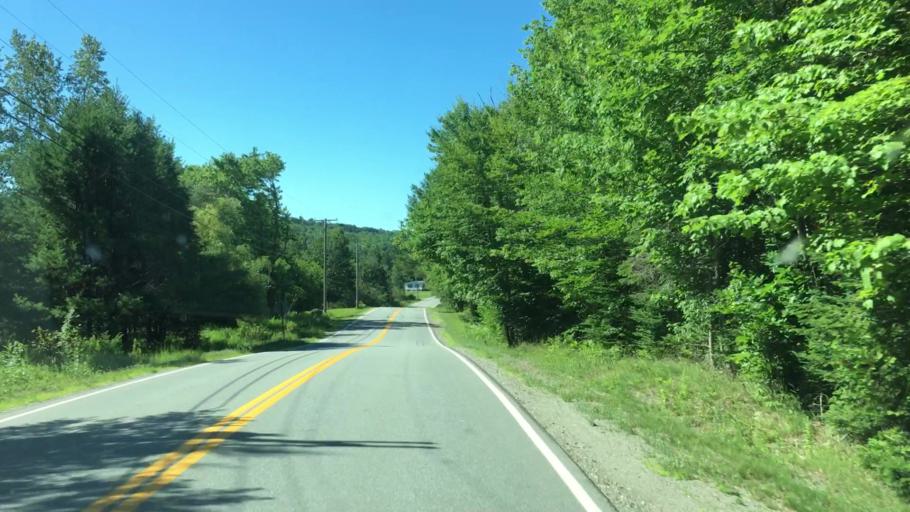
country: US
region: Maine
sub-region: Hancock County
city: Dedham
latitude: 44.7240
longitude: -68.6393
